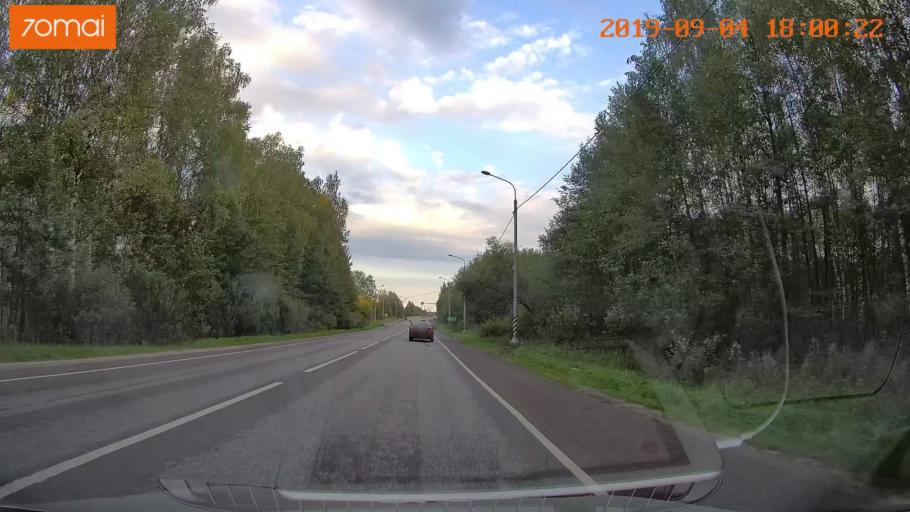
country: RU
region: Moskovskaya
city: Il'inskiy Pogost
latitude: 55.4911
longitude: 38.8606
